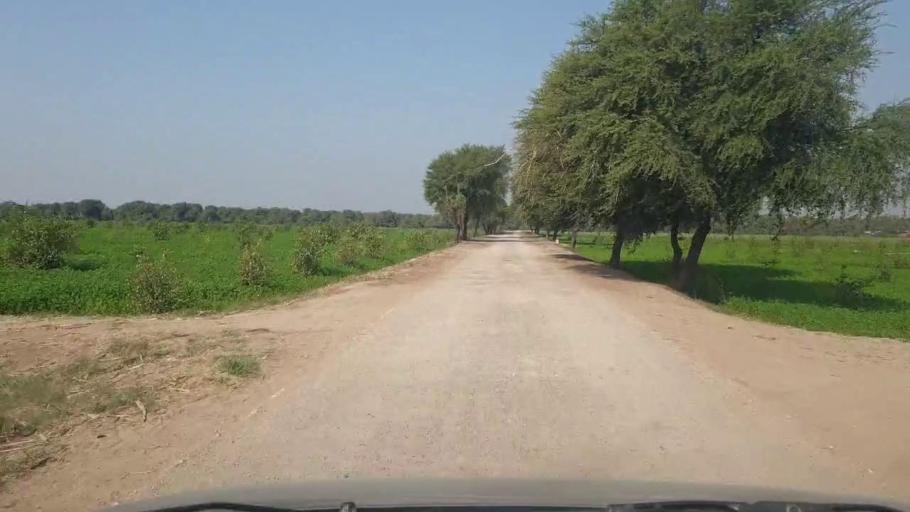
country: PK
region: Sindh
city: Mirwah Gorchani
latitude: 25.2558
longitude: 69.0937
